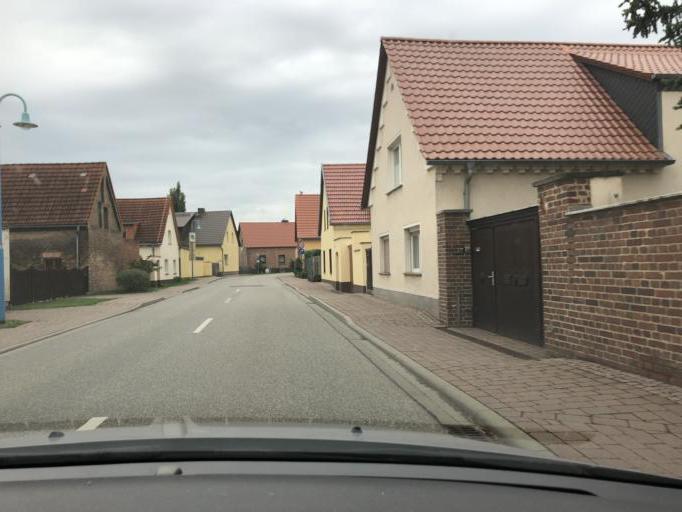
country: DE
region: Saxony-Anhalt
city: Uichteritz
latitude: 51.2071
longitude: 11.9267
